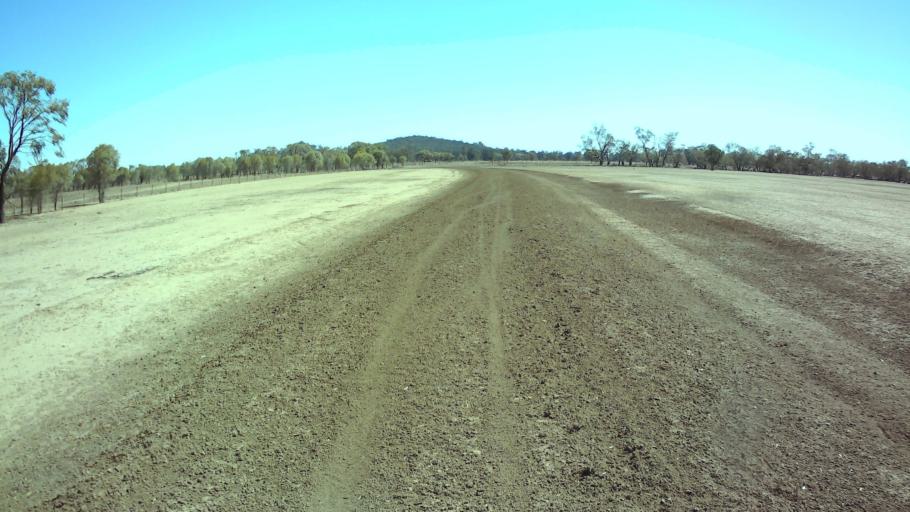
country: AU
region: New South Wales
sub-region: Bland
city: West Wyalong
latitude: -33.7531
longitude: 147.6594
